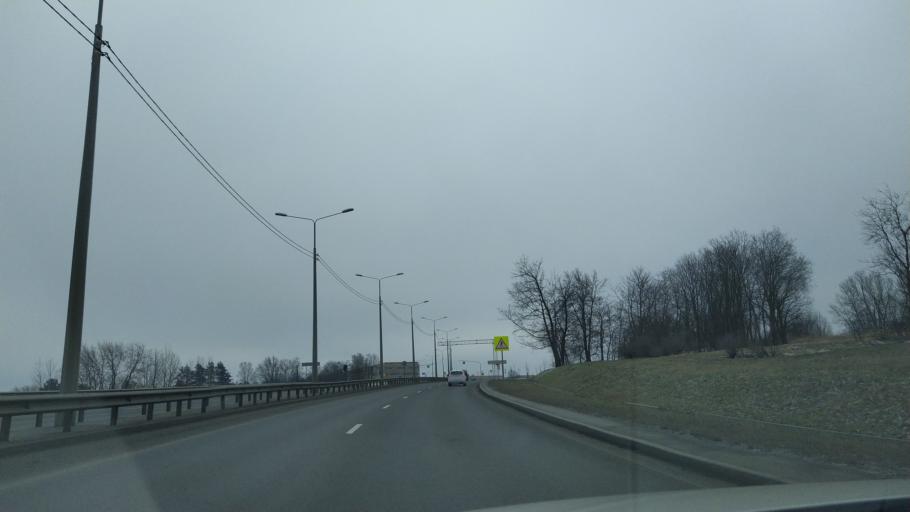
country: RU
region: St.-Petersburg
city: Aleksandrovskaya
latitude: 59.7710
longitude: 30.3436
